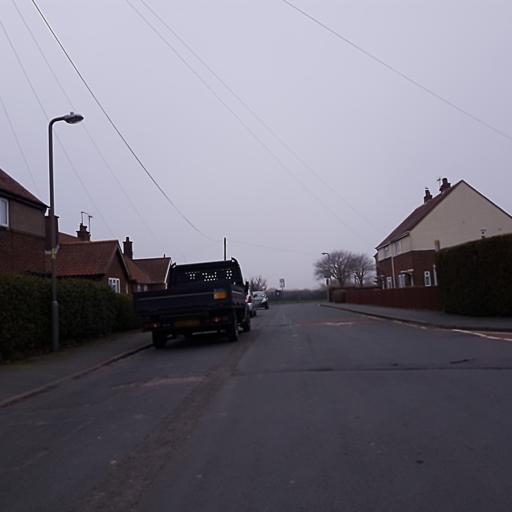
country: GB
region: England
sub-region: North Yorkshire
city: Filey
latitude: 54.2120
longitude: -0.2954
